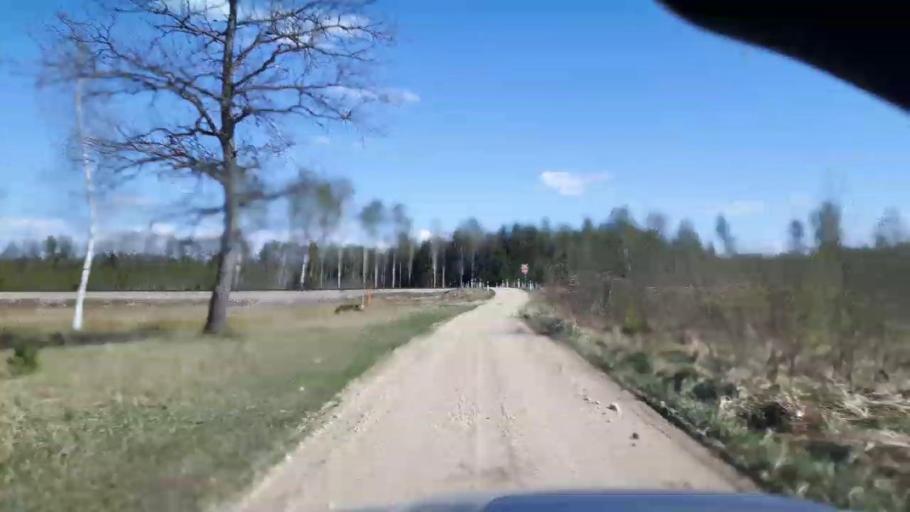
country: EE
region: Paernumaa
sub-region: Tootsi vald
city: Tootsi
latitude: 58.5410
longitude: 24.8119
